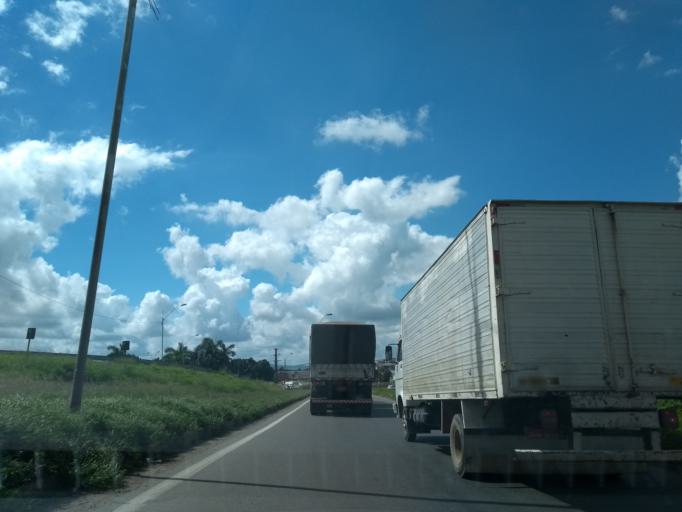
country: BR
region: Bahia
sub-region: Feira De Santana
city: Feira de Santana
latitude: -12.2733
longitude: -38.9362
